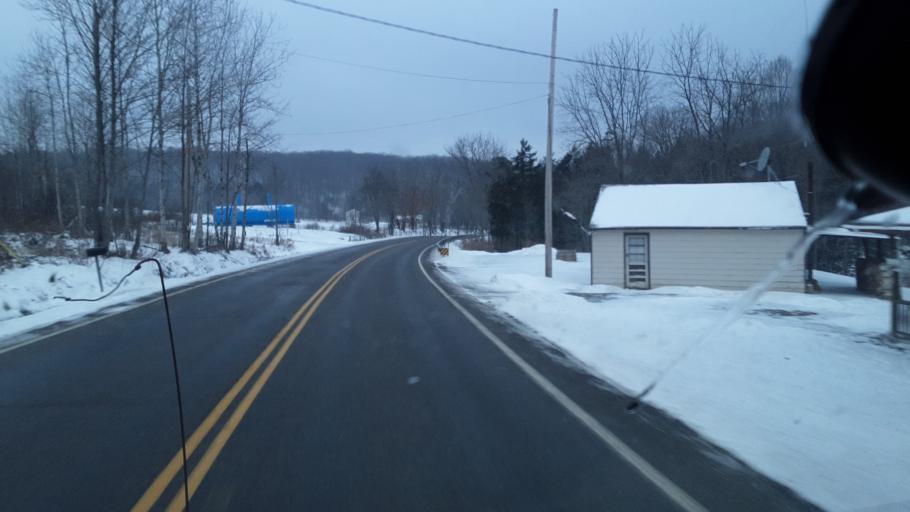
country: US
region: New York
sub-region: Allegany County
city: Andover
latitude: 42.0651
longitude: -77.8289
